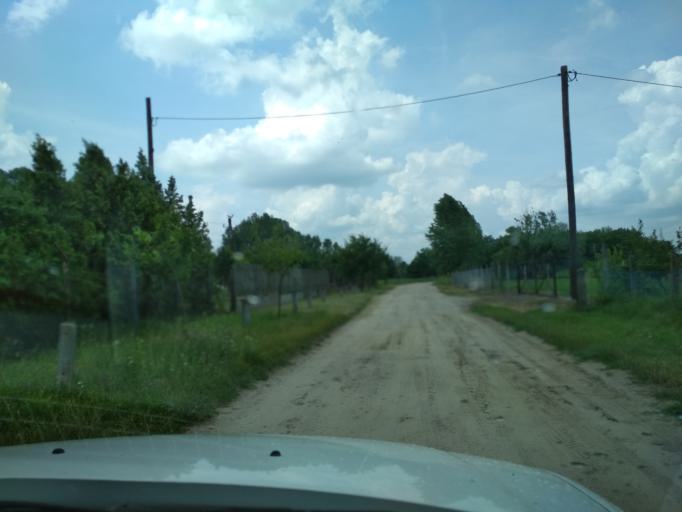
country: HU
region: Pest
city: Nagykata
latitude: 47.4000
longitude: 19.7659
